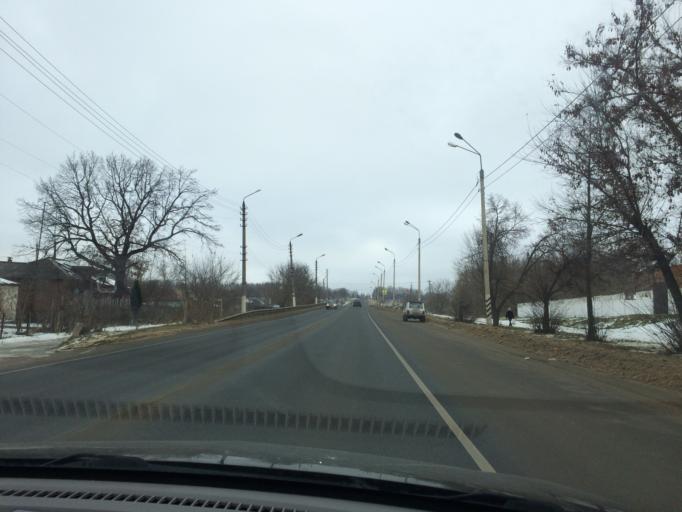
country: RU
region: Tula
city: Plavsk
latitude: 53.7150
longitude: 37.2969
